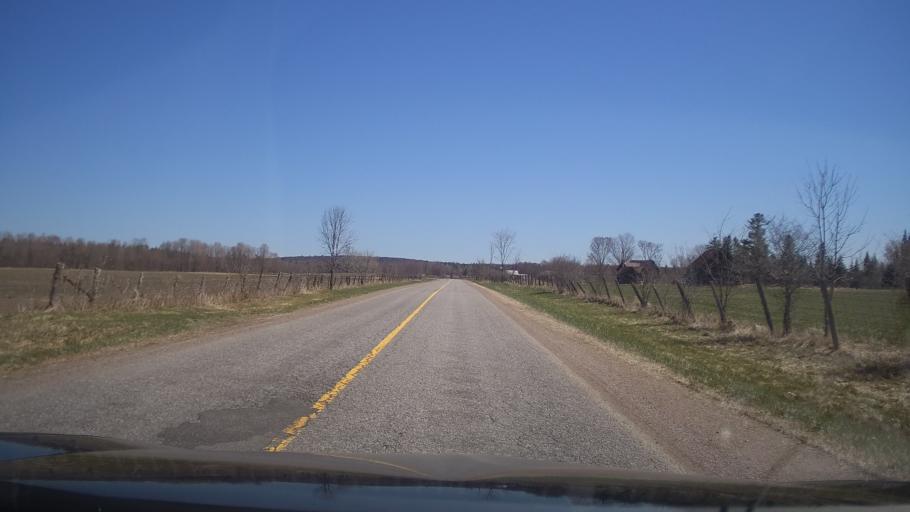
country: CA
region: Quebec
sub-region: Outaouais
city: Shawville
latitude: 45.5457
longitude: -76.3883
